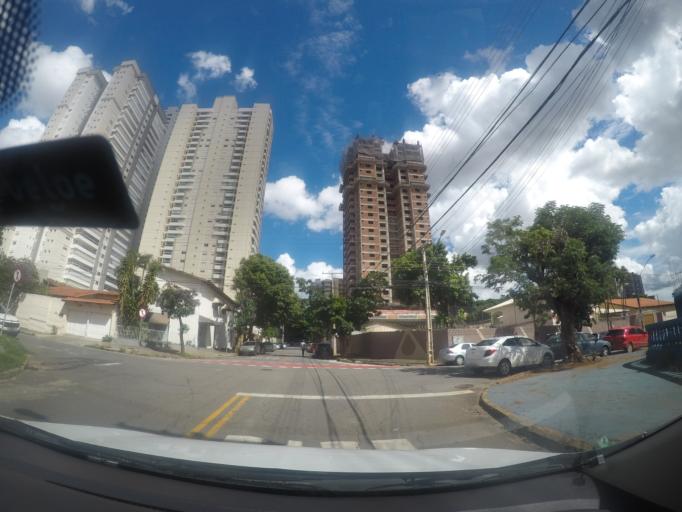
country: BR
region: Goias
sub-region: Goiania
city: Goiania
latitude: -16.6989
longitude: -49.2714
